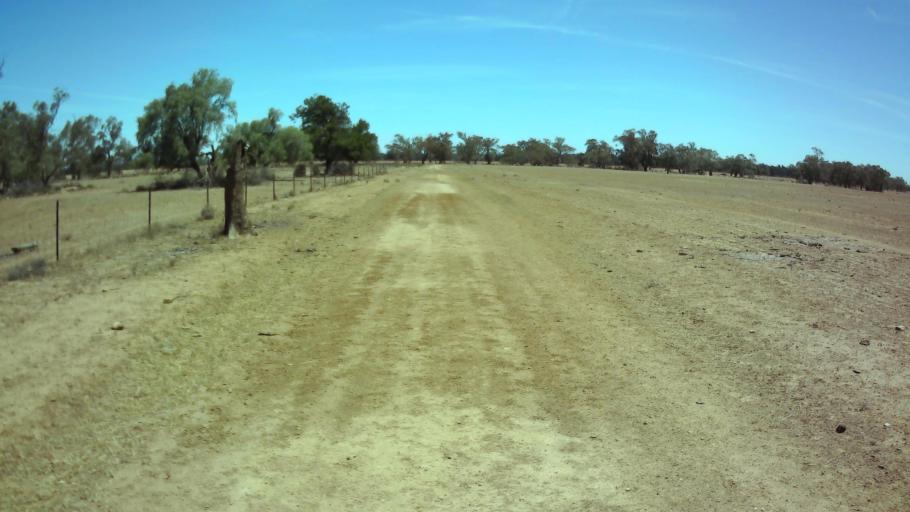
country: AU
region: New South Wales
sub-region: Bland
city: West Wyalong
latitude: -33.8335
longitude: 147.6352
